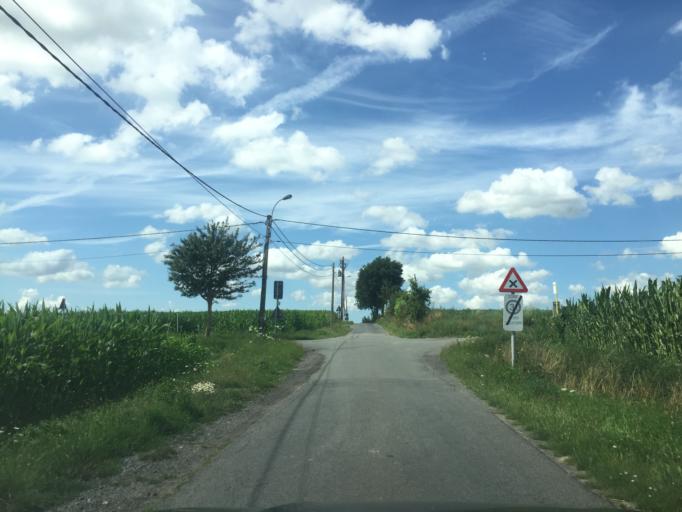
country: BE
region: Flanders
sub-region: Provincie West-Vlaanderen
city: Staden
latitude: 50.9498
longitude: 3.0085
